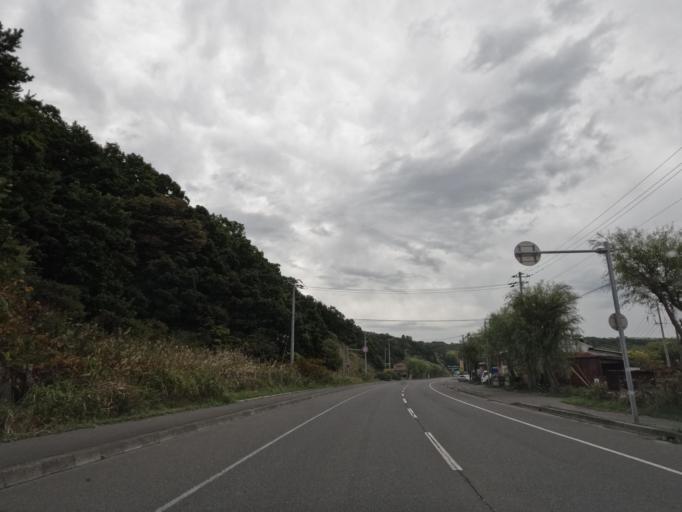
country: JP
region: Hokkaido
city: Muroran
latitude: 42.3728
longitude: 140.9172
